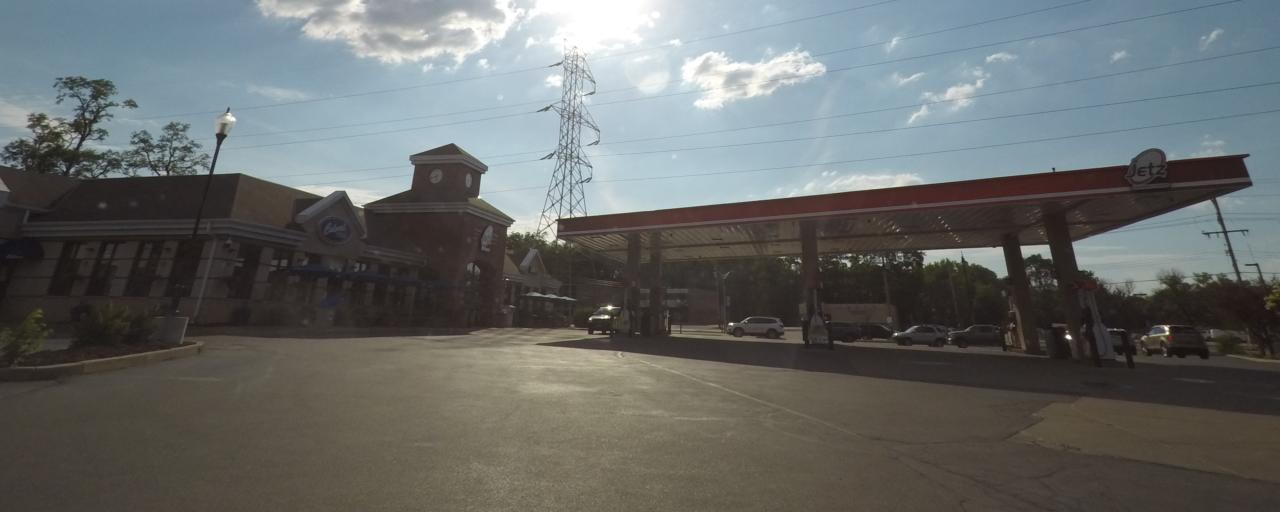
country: US
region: Wisconsin
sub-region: Milwaukee County
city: Hales Corners
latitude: 42.9344
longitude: -88.0491
